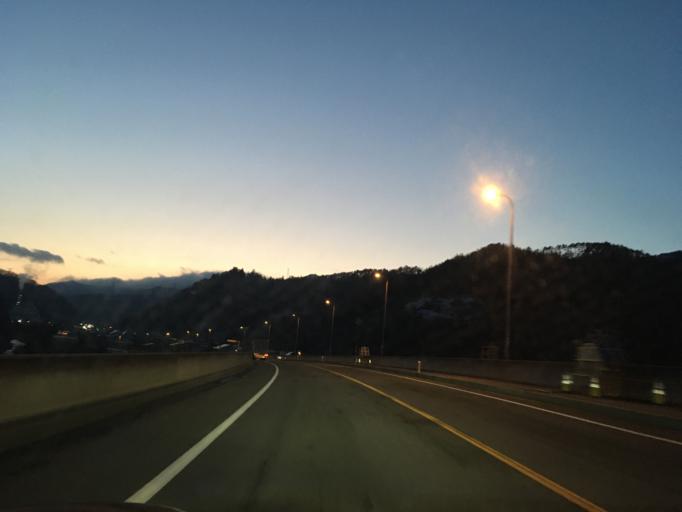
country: JP
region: Yamagata
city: Kaminoyama
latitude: 38.1301
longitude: 140.2483
